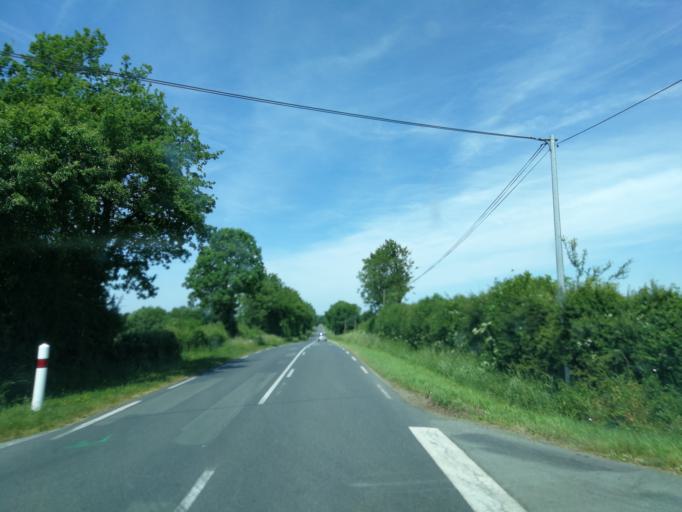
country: FR
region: Poitou-Charentes
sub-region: Departement des Deux-Sevres
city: La Foret-sur-Sevre
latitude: 46.7338
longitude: -0.6698
